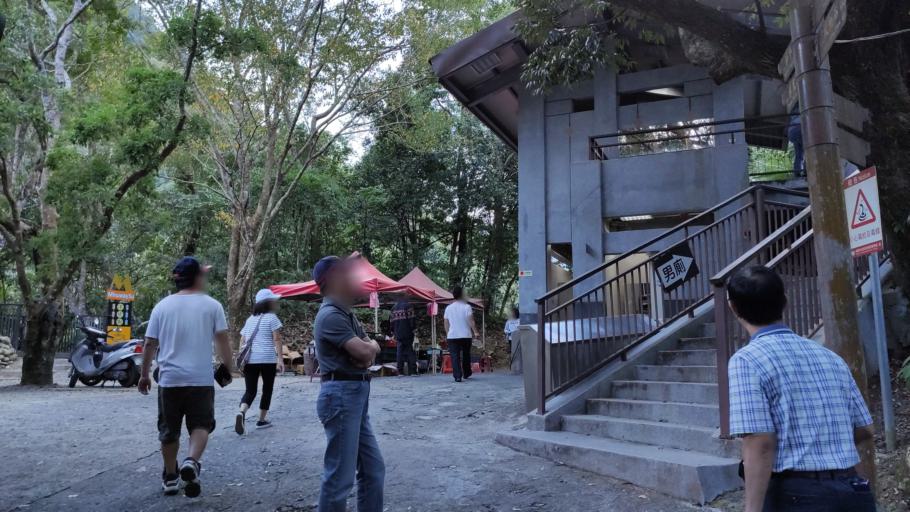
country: TW
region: Taiwan
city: Daxi
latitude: 24.7900
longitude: 121.3750
